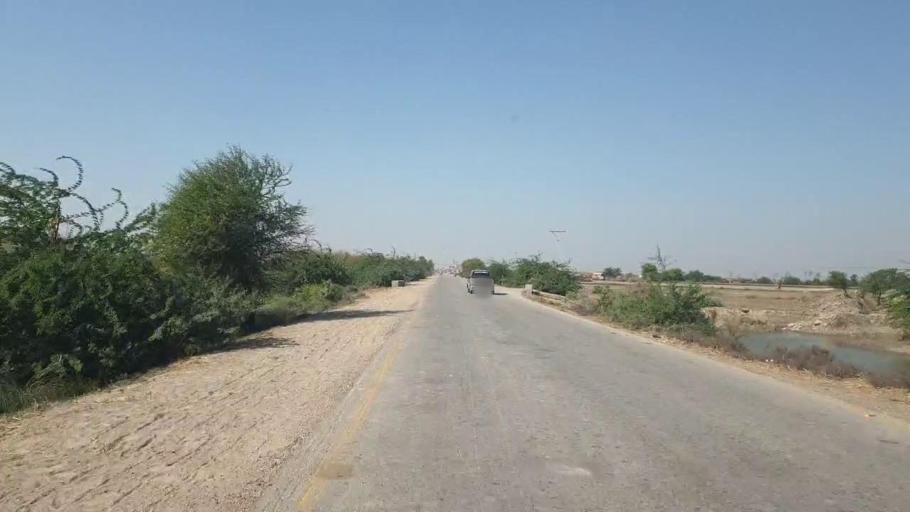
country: PK
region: Sindh
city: Rajo Khanani
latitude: 25.0569
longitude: 68.8032
